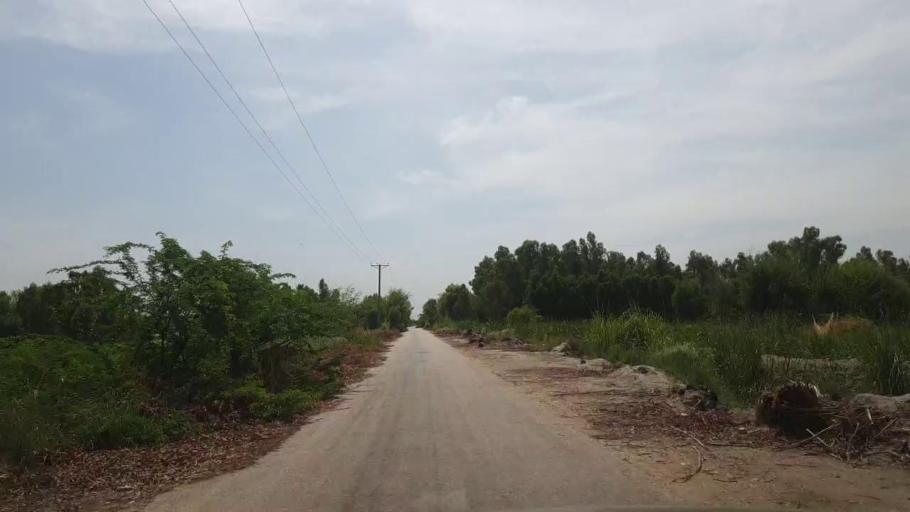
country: PK
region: Sindh
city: Kot Diji
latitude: 27.1202
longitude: 69.0029
